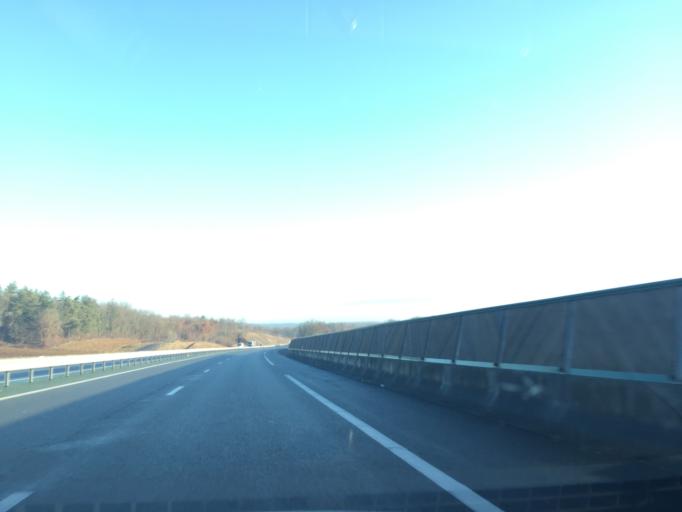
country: FR
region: Aquitaine
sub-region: Departement de la Dordogne
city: Thenon
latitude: 45.1711
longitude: 0.9557
